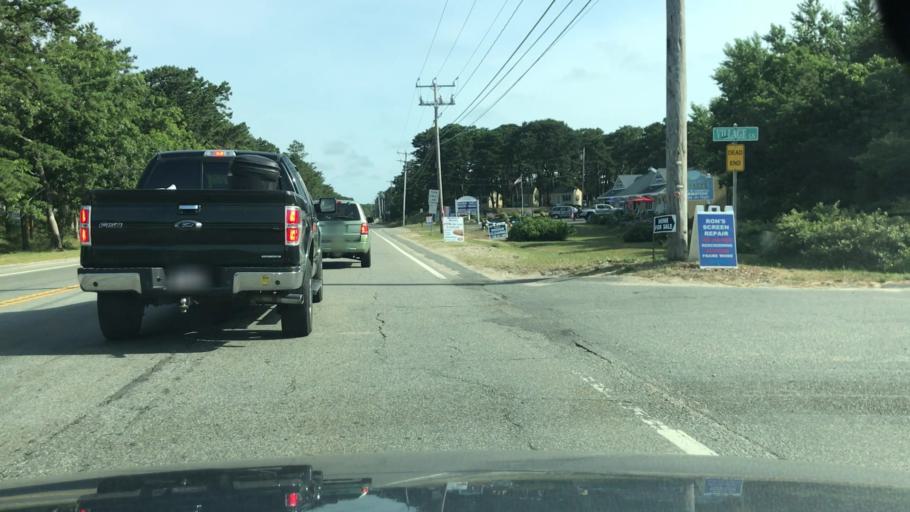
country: US
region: Massachusetts
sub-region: Barnstable County
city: North Eastham
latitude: 41.8785
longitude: -69.9879
